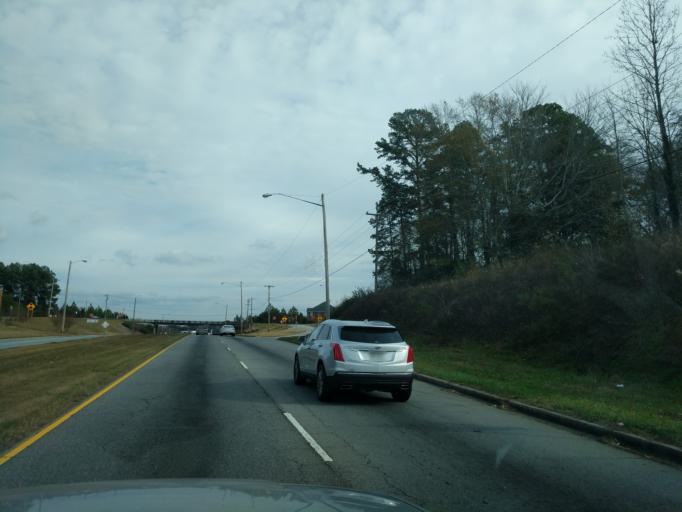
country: US
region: South Carolina
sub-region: Oconee County
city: Seneca
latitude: 34.6976
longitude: -82.9632
